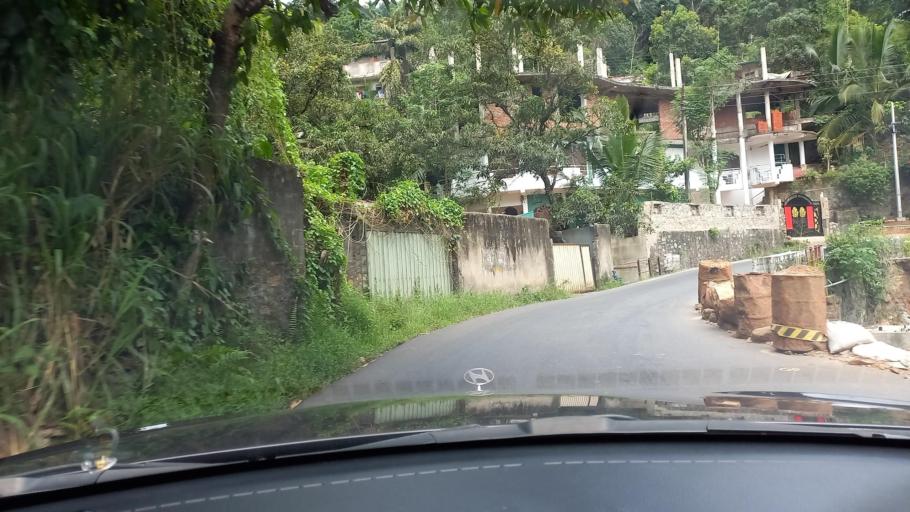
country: LK
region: Central
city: Kandy
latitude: 7.2320
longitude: 80.6058
